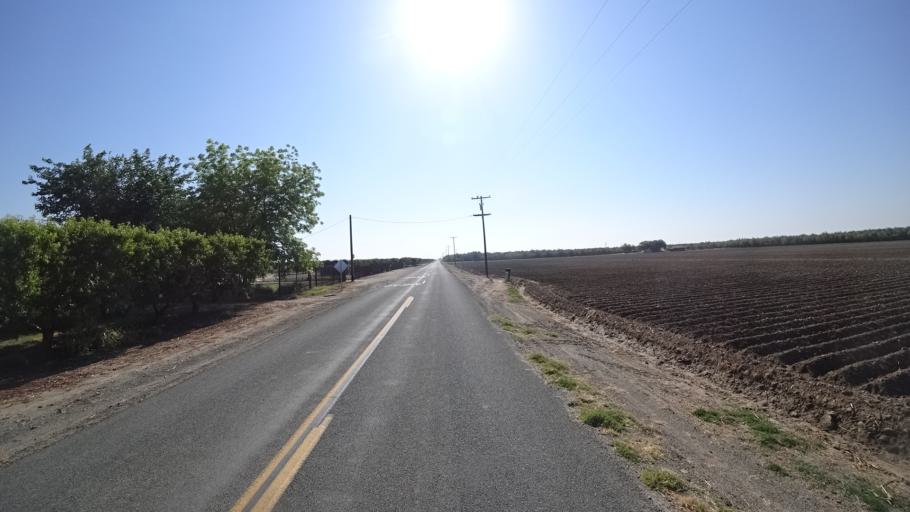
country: US
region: California
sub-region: Kings County
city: Lucerne
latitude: 36.3866
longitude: -119.5818
